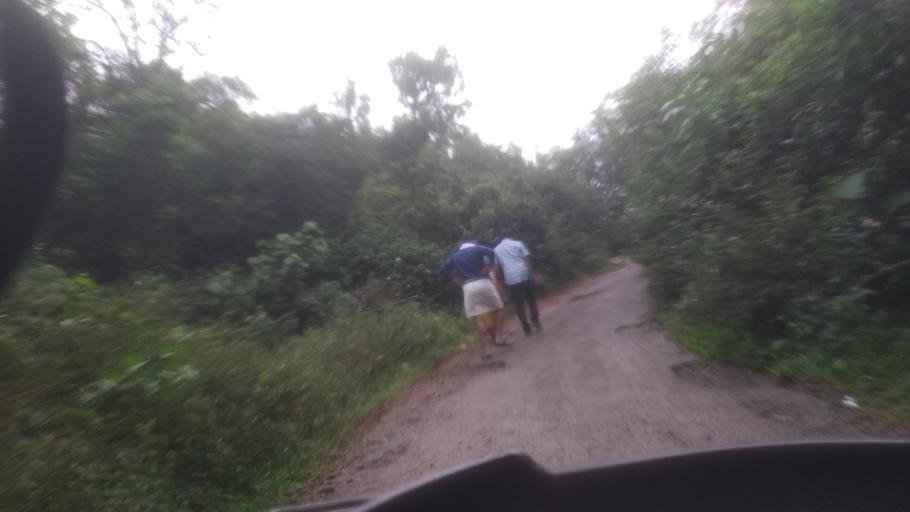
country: IN
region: Tamil Nadu
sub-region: Theni
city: Kombai
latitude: 9.8910
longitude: 77.2180
